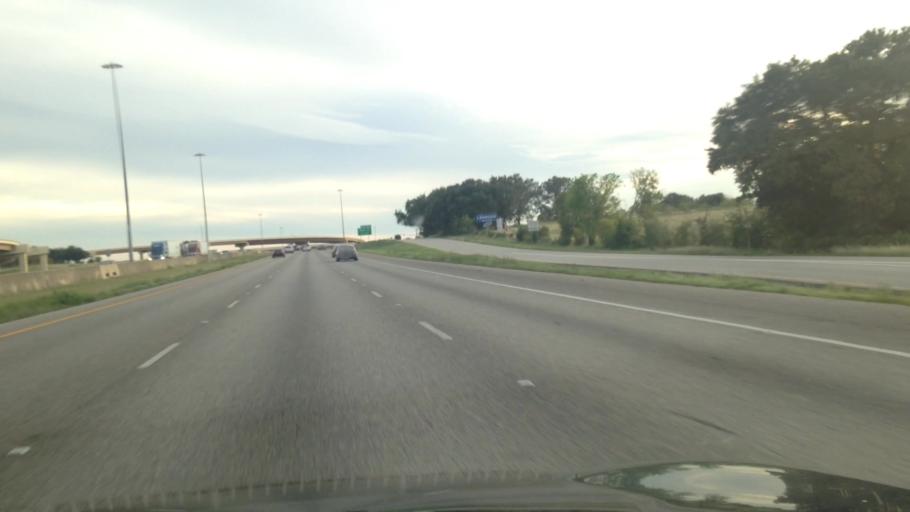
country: US
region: Texas
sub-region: Travis County
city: Onion Creek
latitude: 30.1179
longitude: -97.8050
